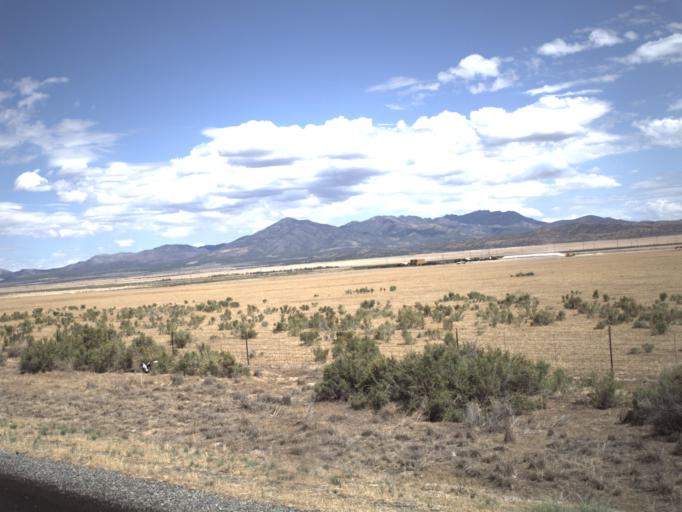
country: US
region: Utah
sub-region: Millard County
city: Fillmore
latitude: 39.1250
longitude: -112.3584
